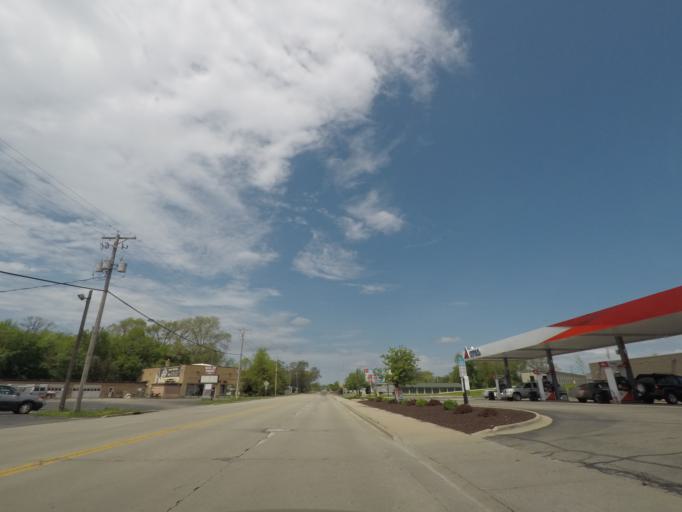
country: US
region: Wisconsin
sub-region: Rock County
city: Beloit
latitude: 42.5155
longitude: -89.0617
